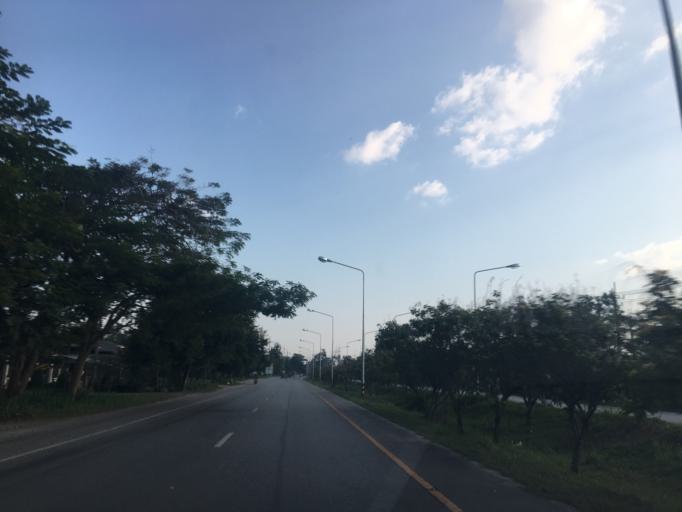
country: TH
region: Phayao
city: Phayao
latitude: 19.1034
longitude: 99.9101
